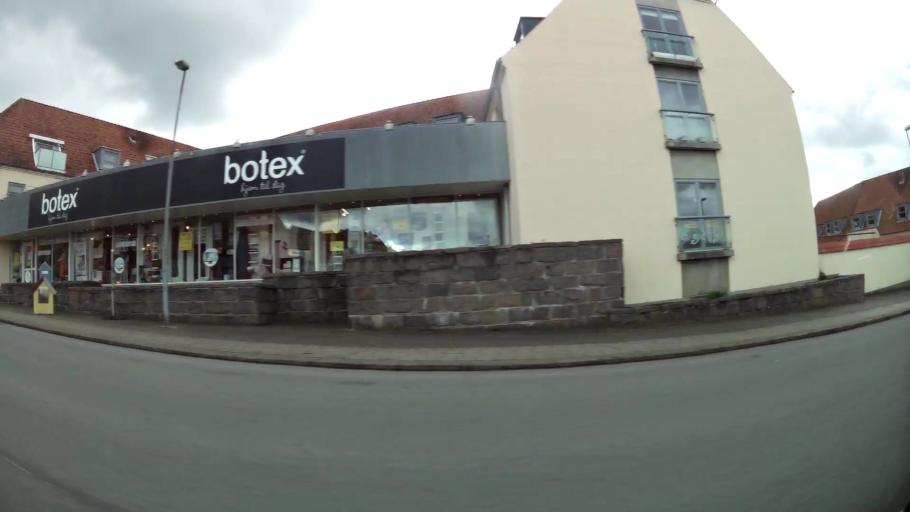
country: DK
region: South Denmark
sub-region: Haderslev Kommune
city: Haderslev
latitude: 55.2519
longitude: 9.4829
